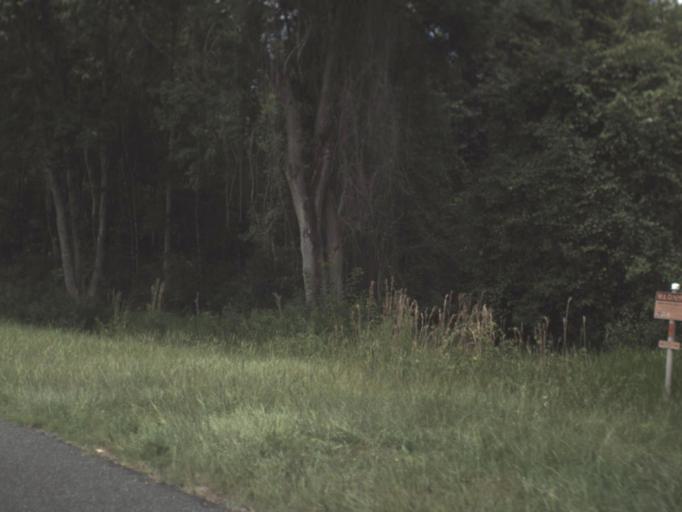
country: US
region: Florida
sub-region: Taylor County
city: Perry
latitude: 30.2087
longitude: -83.6623
